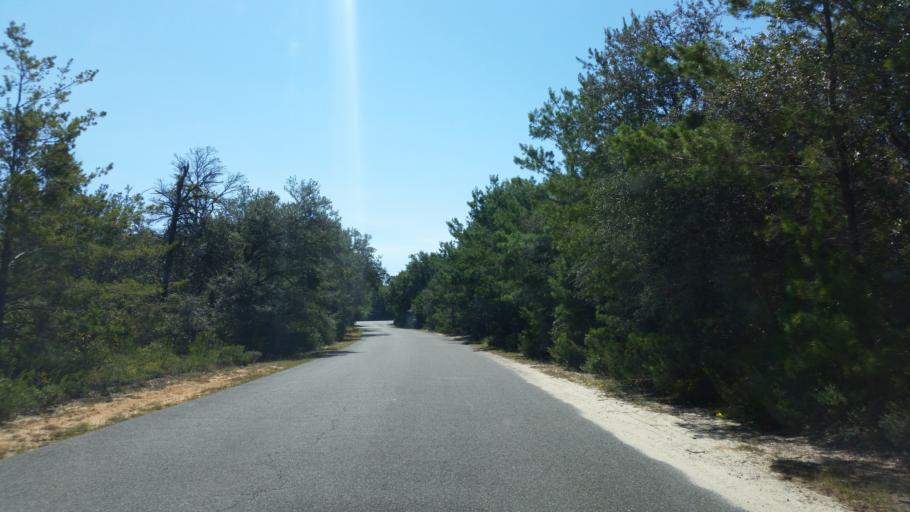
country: US
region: Florida
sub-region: Santa Rosa County
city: Gulf Breeze
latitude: 30.3649
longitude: -87.1394
